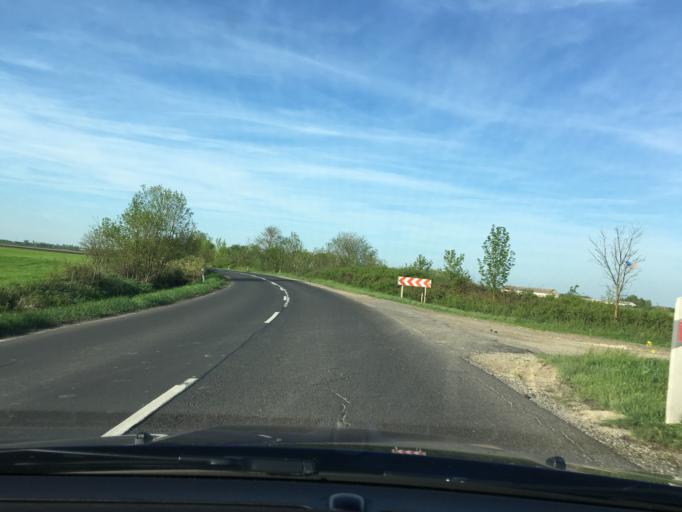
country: HU
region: Bekes
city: Korosladany
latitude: 46.9209
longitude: 21.0747
